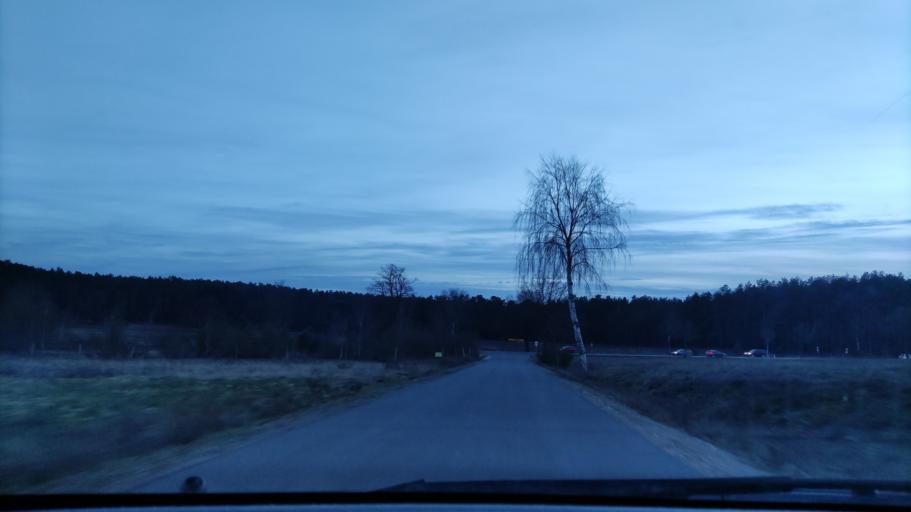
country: DE
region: Lower Saxony
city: Gohrde
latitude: 53.1518
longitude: 10.8457
